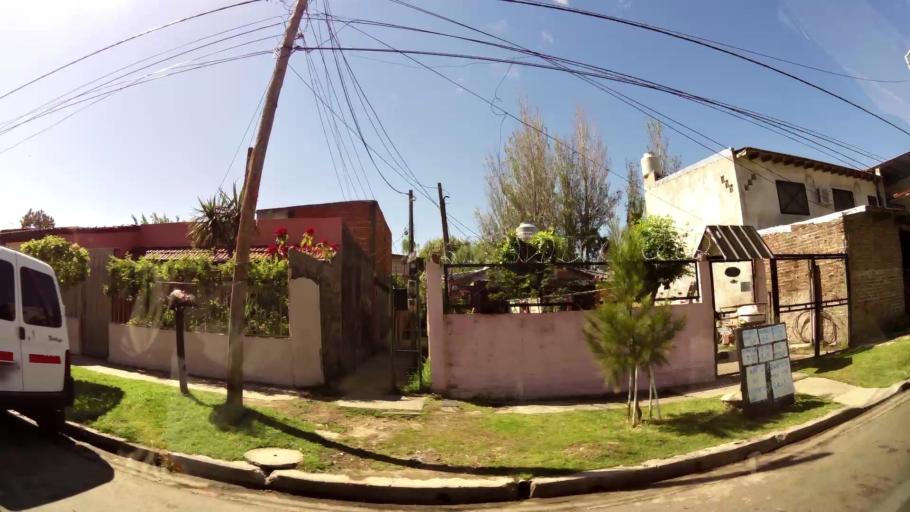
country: AR
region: Buenos Aires
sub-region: Partido de Avellaneda
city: Avellaneda
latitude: -34.6854
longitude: -58.3092
